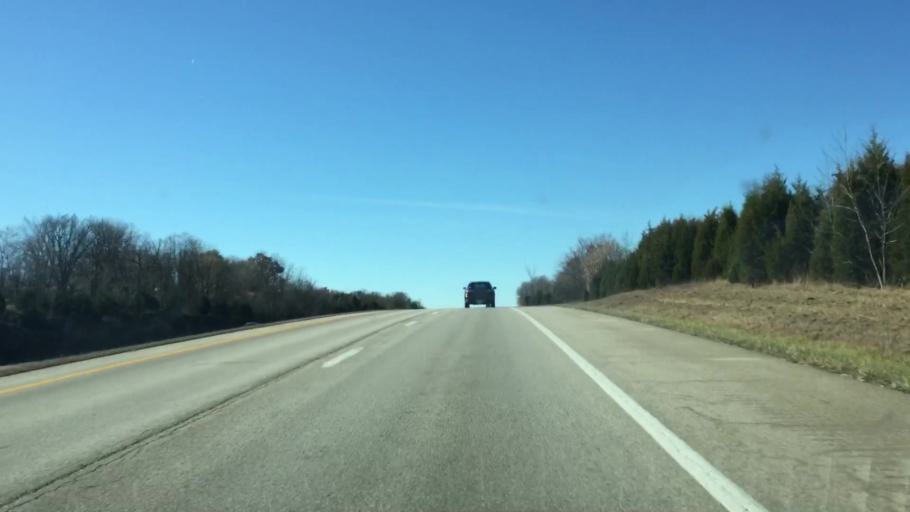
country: US
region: Missouri
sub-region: Cole County
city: Saint Martins
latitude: 38.4097
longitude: -92.3531
